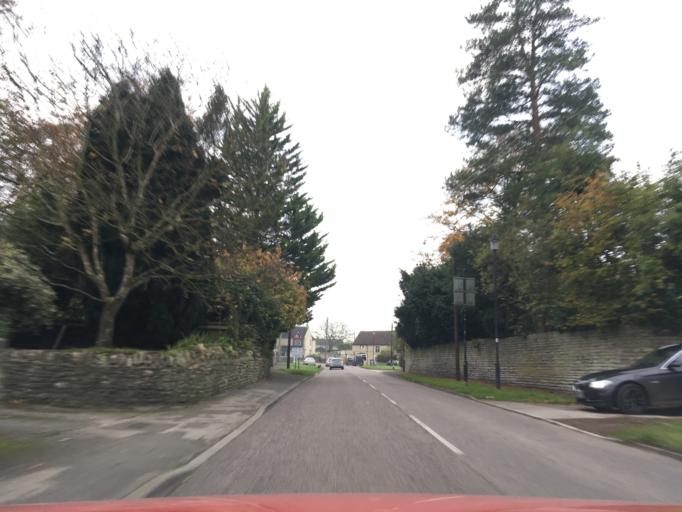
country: GB
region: England
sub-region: South Gloucestershire
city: Pucklechurch
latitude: 51.4881
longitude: -2.4343
